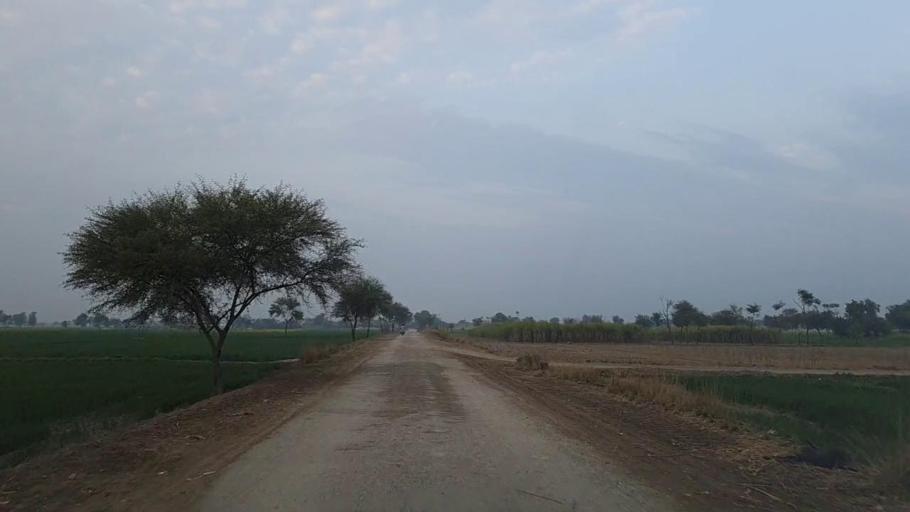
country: PK
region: Sindh
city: Jam Sahib
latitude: 26.2949
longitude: 68.5934
